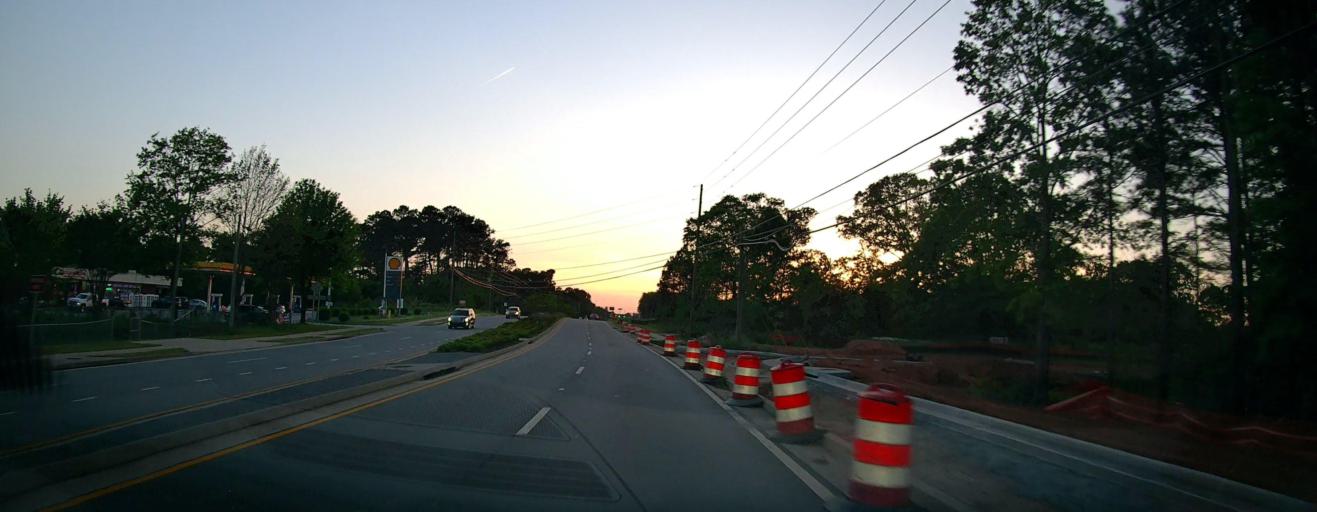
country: US
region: Georgia
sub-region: Henry County
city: McDonough
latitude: 33.4830
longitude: -84.2008
